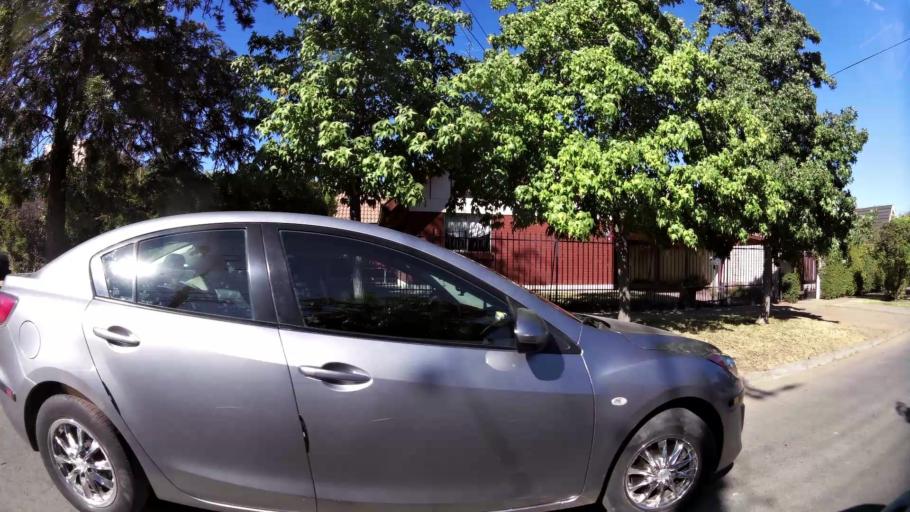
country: CL
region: O'Higgins
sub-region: Provincia de Cachapoal
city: Rancagua
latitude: -34.1827
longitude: -70.7198
